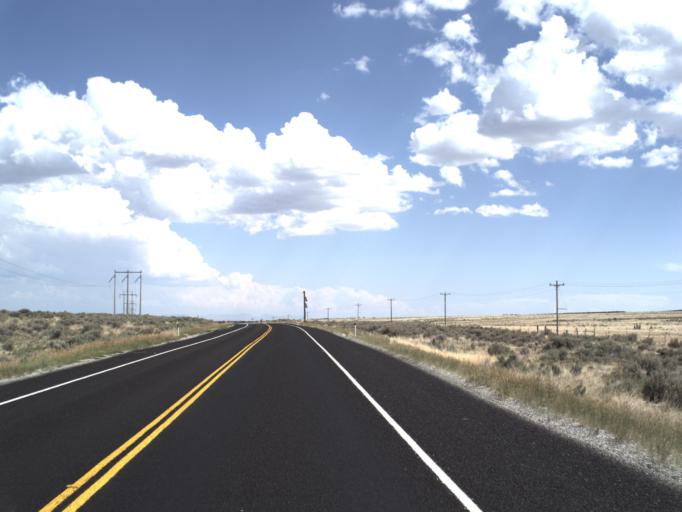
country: US
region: Idaho
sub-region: Minidoka County
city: Rupert
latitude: 41.9952
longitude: -113.1902
